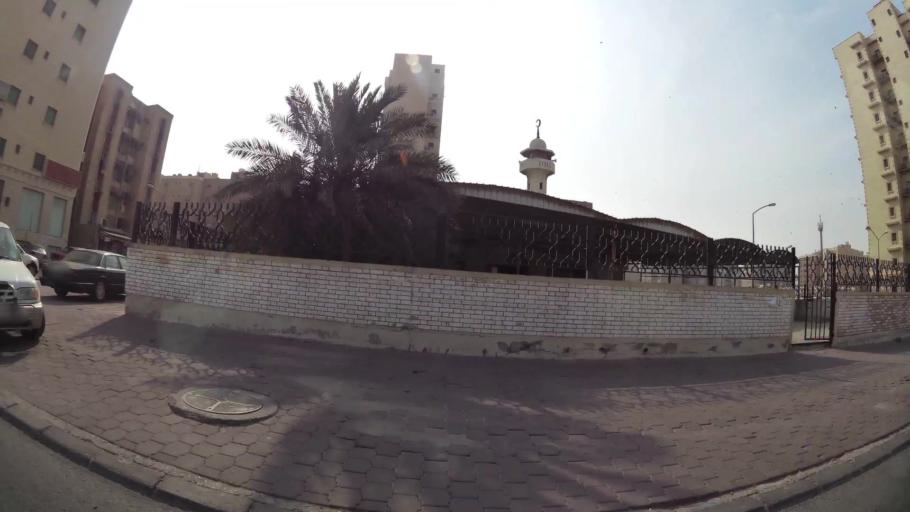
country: KW
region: Al Farwaniyah
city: Al Farwaniyah
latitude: 29.2752
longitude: 47.9603
